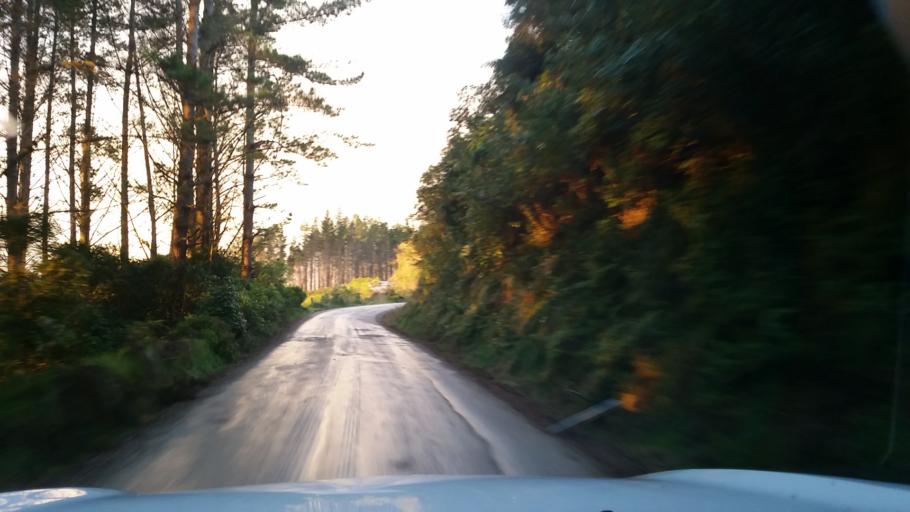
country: NZ
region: Manawatu-Wanganui
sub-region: Wanganui District
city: Wanganui
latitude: -39.7747
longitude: 174.8596
